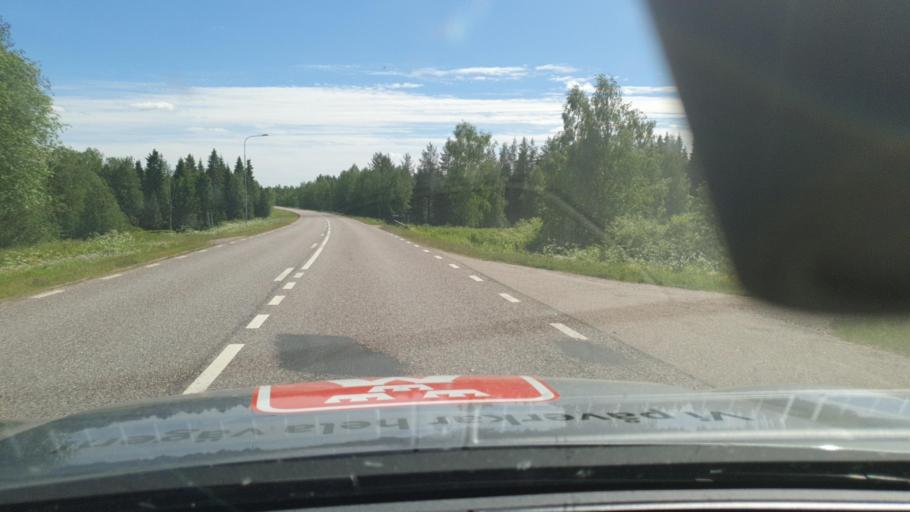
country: FI
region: Lapland
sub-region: Torniolaakso
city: Pello
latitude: 66.9991
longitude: 23.7596
